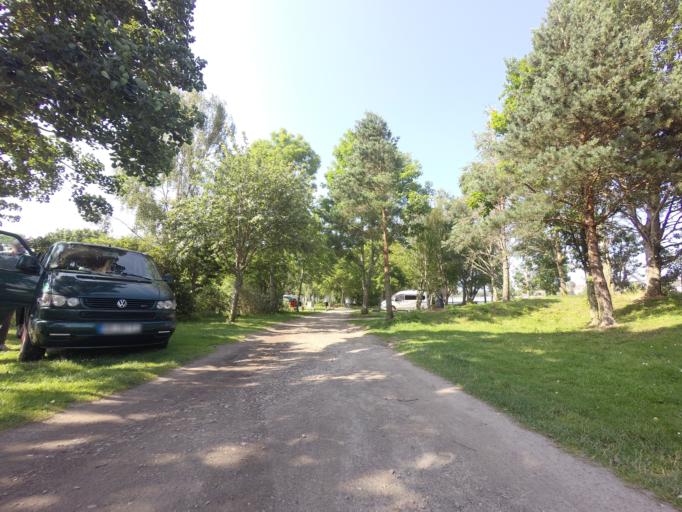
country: GB
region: Scotland
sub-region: Highland
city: Alness
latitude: 57.8904
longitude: -4.3483
